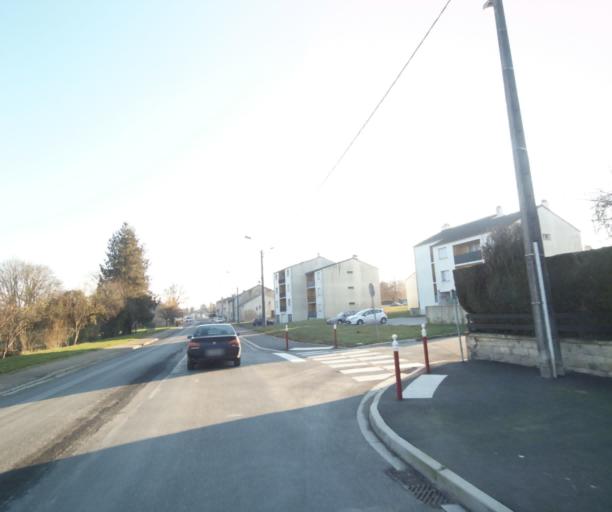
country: FR
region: Champagne-Ardenne
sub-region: Departement de la Haute-Marne
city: Chevillon
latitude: 48.5302
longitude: 5.0974
